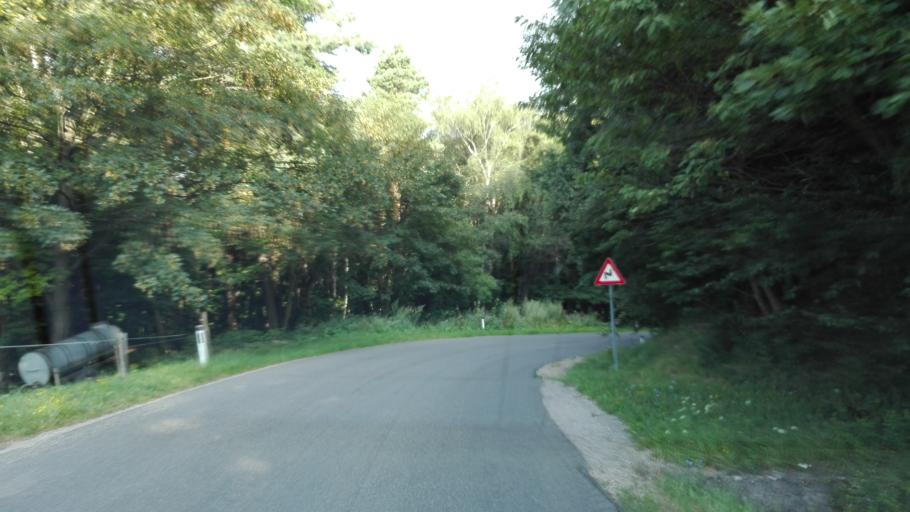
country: AT
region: Lower Austria
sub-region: Politischer Bezirk Sankt Polten
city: Stossing
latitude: 48.0958
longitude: 15.8200
